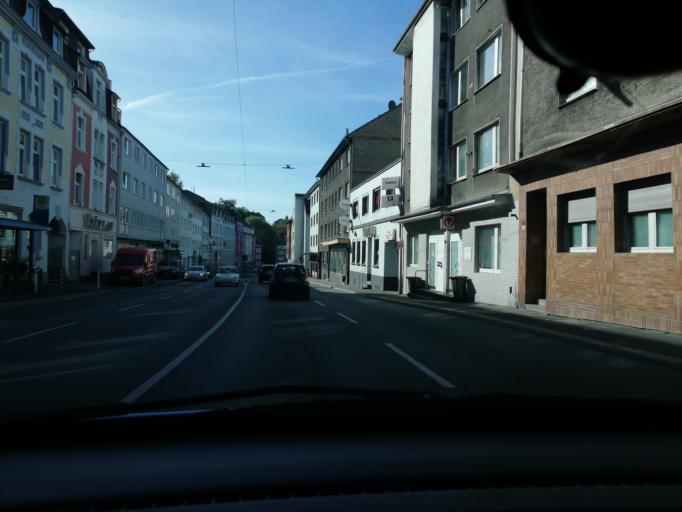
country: DE
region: North Rhine-Westphalia
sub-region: Regierungsbezirk Dusseldorf
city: Wuppertal
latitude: 51.2816
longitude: 7.2065
